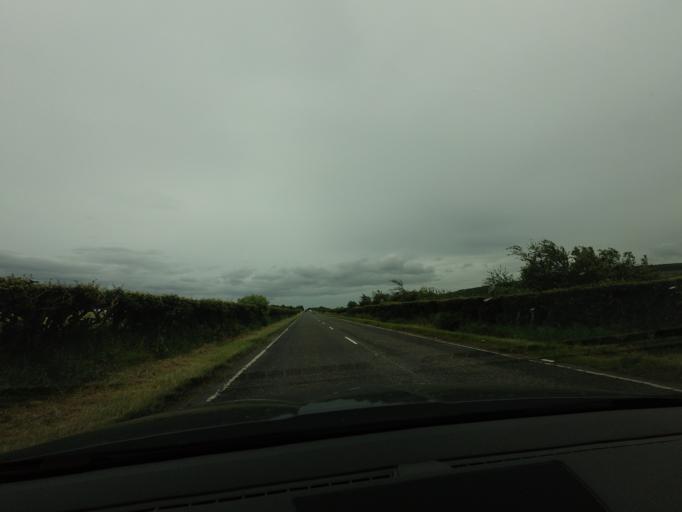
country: GB
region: Scotland
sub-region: Moray
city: Buckie
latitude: 57.6652
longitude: -2.9449
